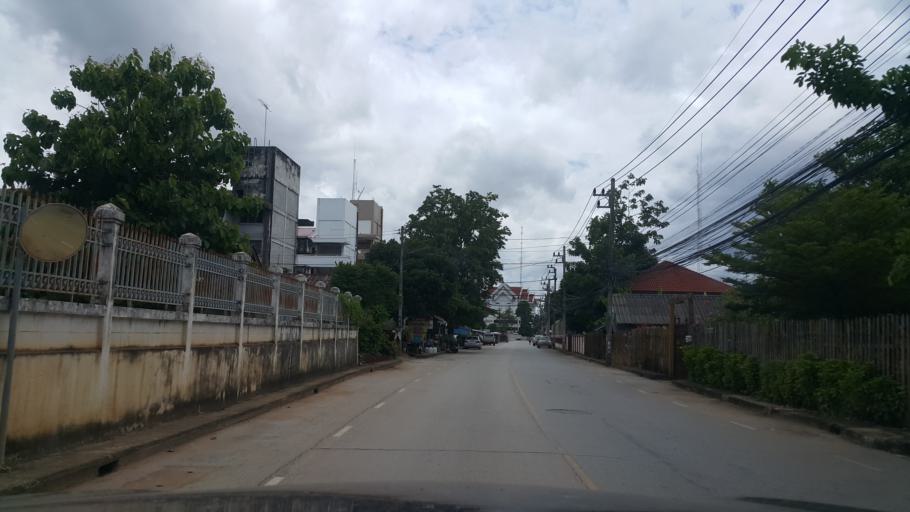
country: TH
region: Sukhothai
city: Sukhothai
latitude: 17.0048
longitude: 99.8307
